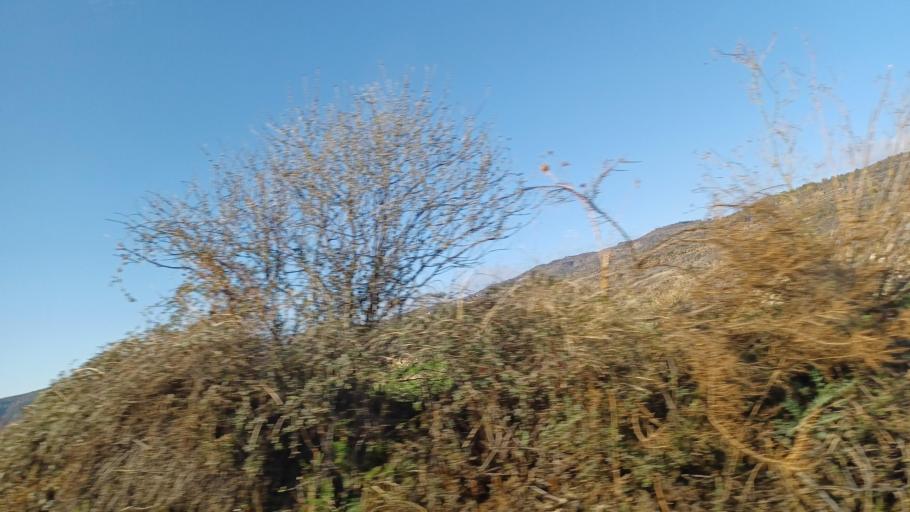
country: CY
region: Limassol
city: Pachna
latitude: 34.8515
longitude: 32.7288
